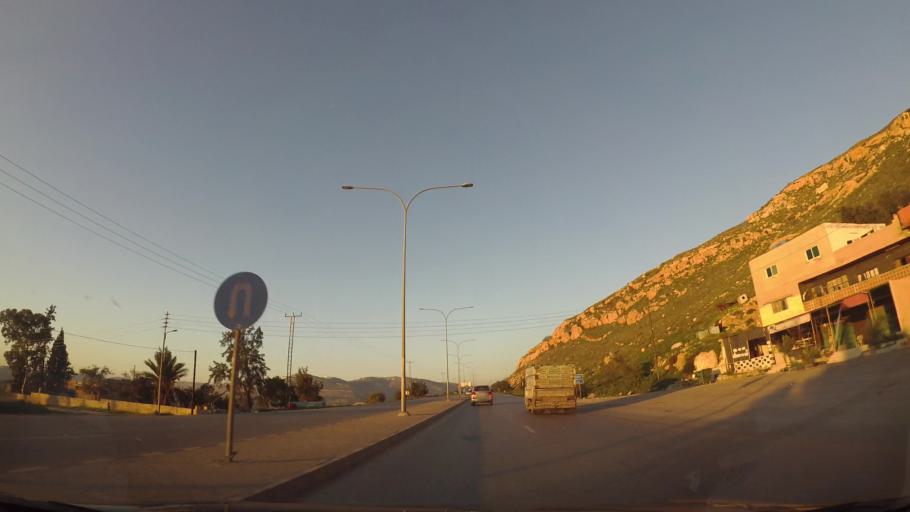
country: JO
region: Amman
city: Umm as Summaq
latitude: 31.8696
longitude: 35.7689
